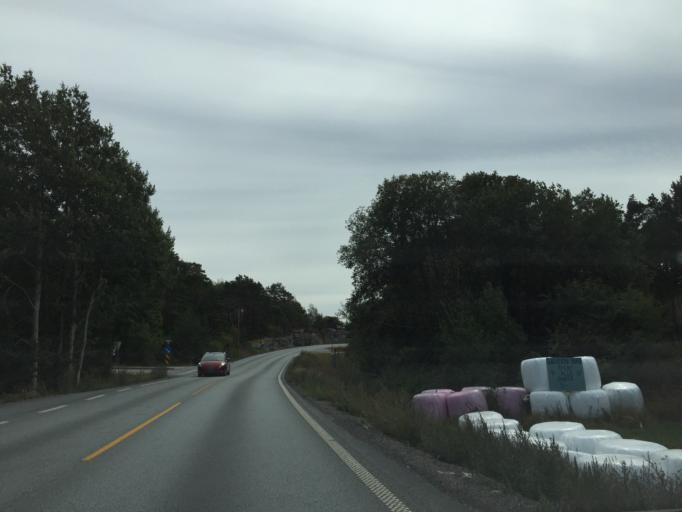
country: NO
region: Ostfold
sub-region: Hvaler
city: Skjaerhalden
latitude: 59.0594
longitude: 10.9436
